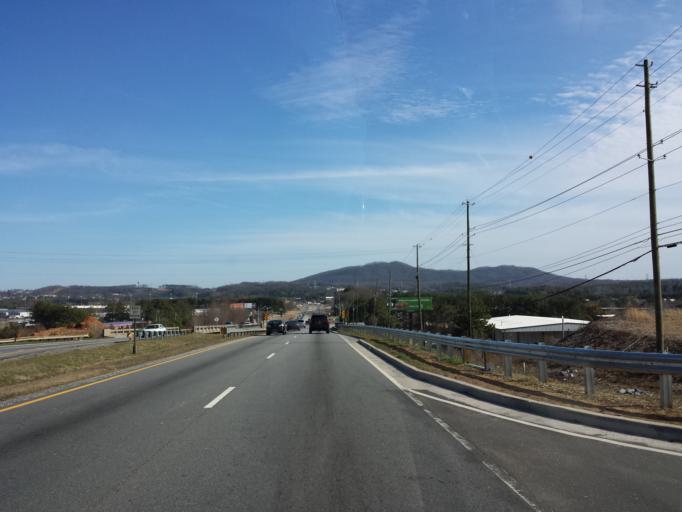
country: US
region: Georgia
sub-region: Cobb County
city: Kennesaw
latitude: 34.0138
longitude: -84.6136
